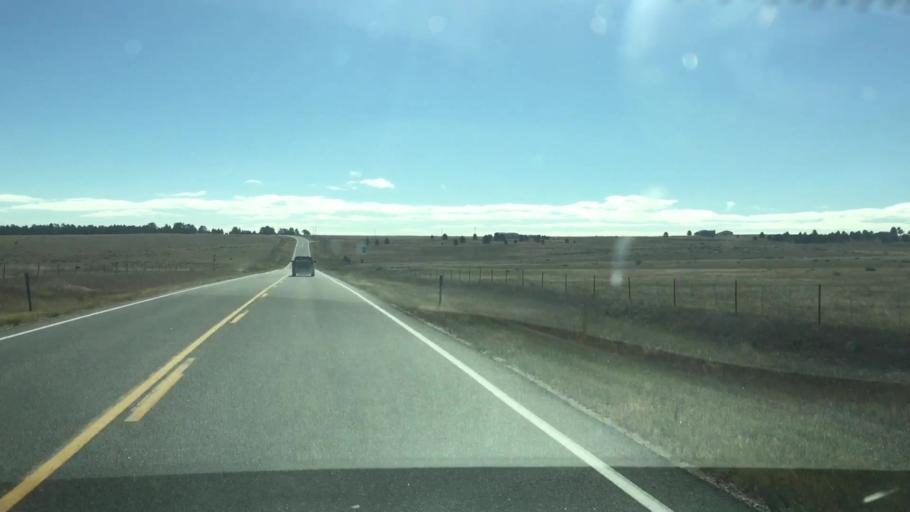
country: US
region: Colorado
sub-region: Elbert County
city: Kiowa
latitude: 39.3362
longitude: -104.4264
